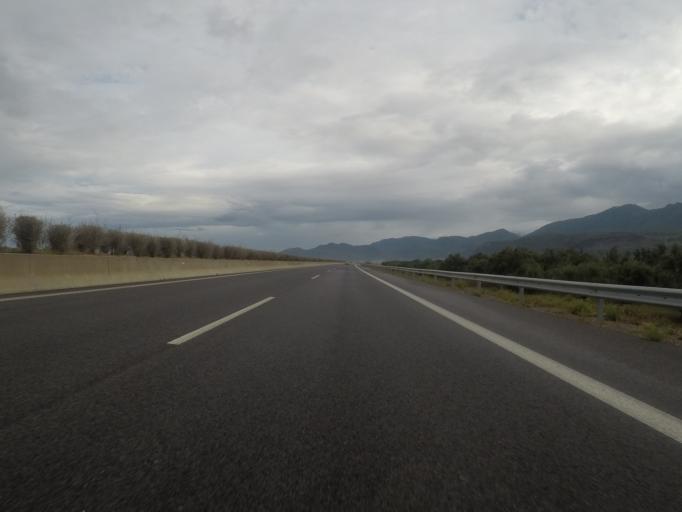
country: GR
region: Peloponnese
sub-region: Nomos Messinias
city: Thouria
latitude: 37.1080
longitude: 22.0343
